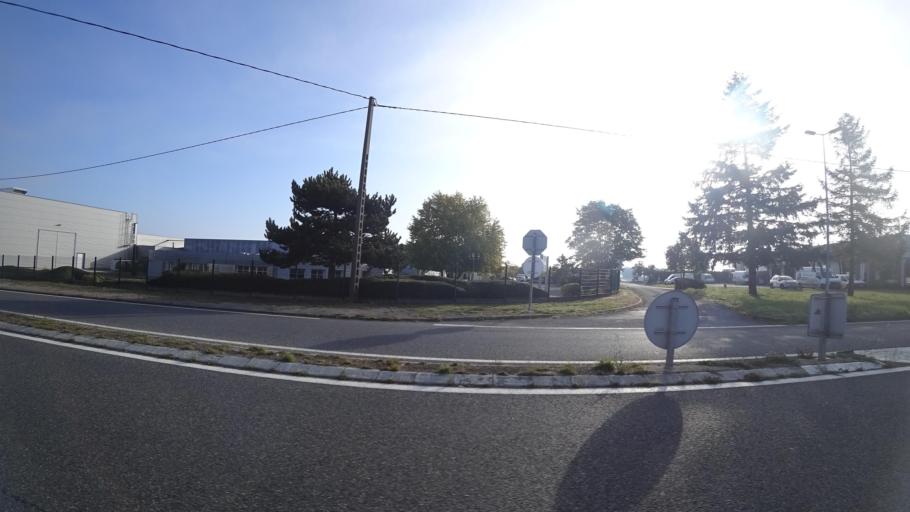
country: FR
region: Midi-Pyrenees
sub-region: Departement de l'Aveyron
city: Luc-la-Primaube
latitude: 44.3228
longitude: 2.5586
